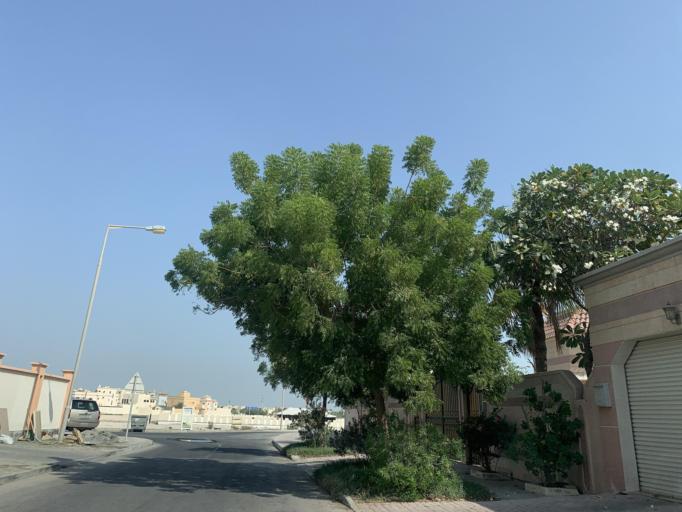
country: BH
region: Central Governorate
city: Madinat Hamad
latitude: 26.1300
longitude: 50.5053
